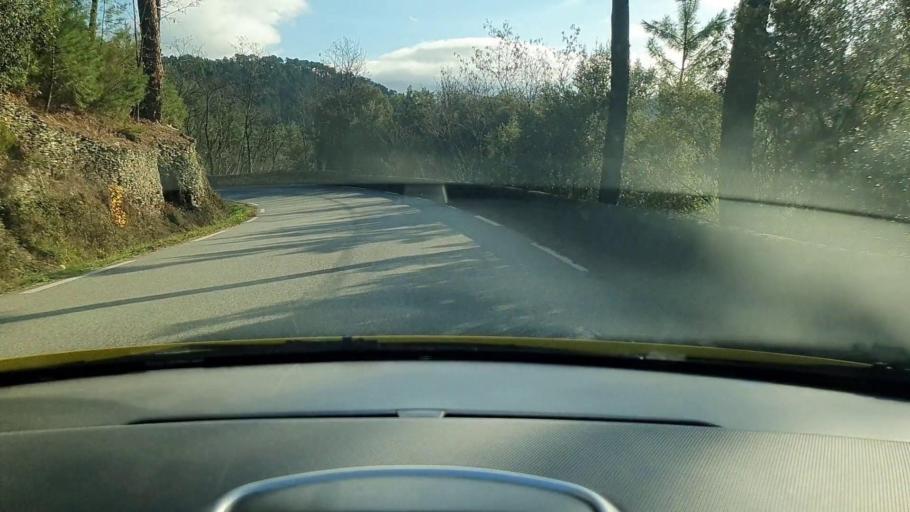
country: FR
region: Languedoc-Roussillon
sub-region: Departement du Gard
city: Branoux-les-Taillades
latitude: 44.3186
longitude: 3.9640
